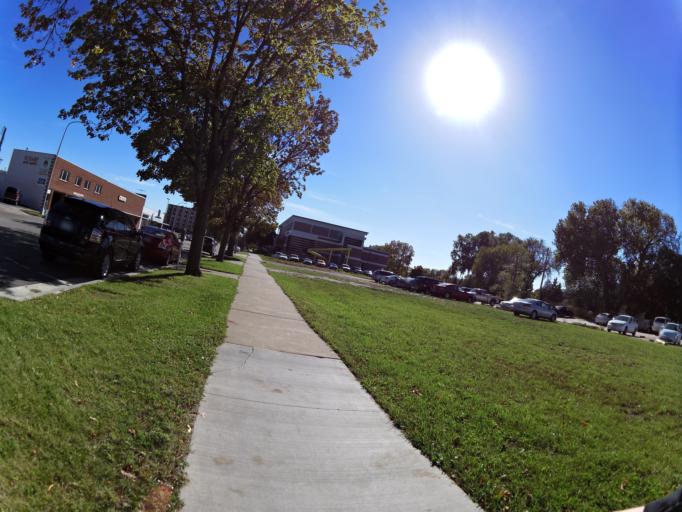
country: US
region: Minnesota
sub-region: Olmsted County
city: Rochester
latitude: 44.0410
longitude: -92.4189
